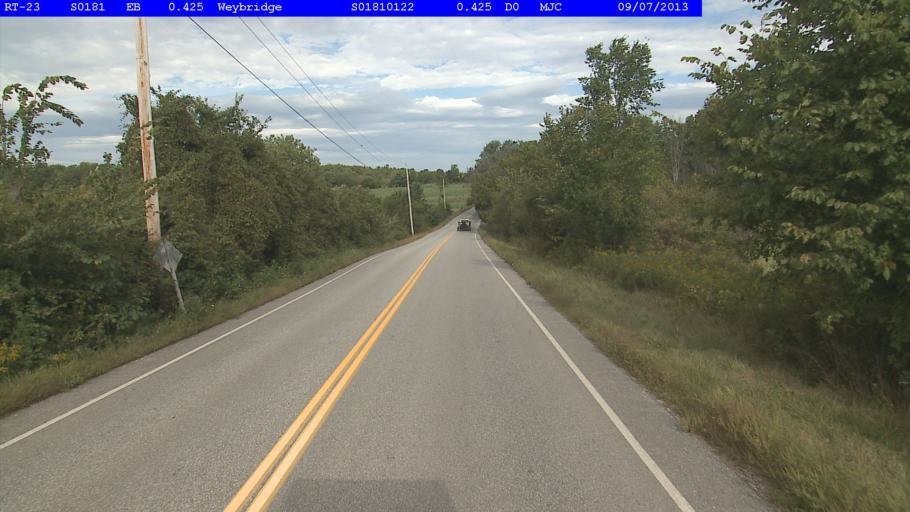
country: US
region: Vermont
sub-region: Addison County
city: Middlebury (village)
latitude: 44.0226
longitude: -73.1894
